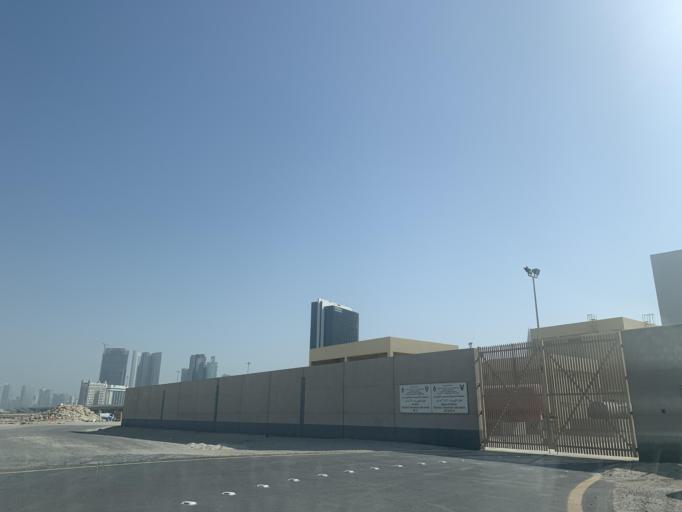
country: BH
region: Muharraq
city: Al Muharraq
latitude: 26.2533
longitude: 50.5852
